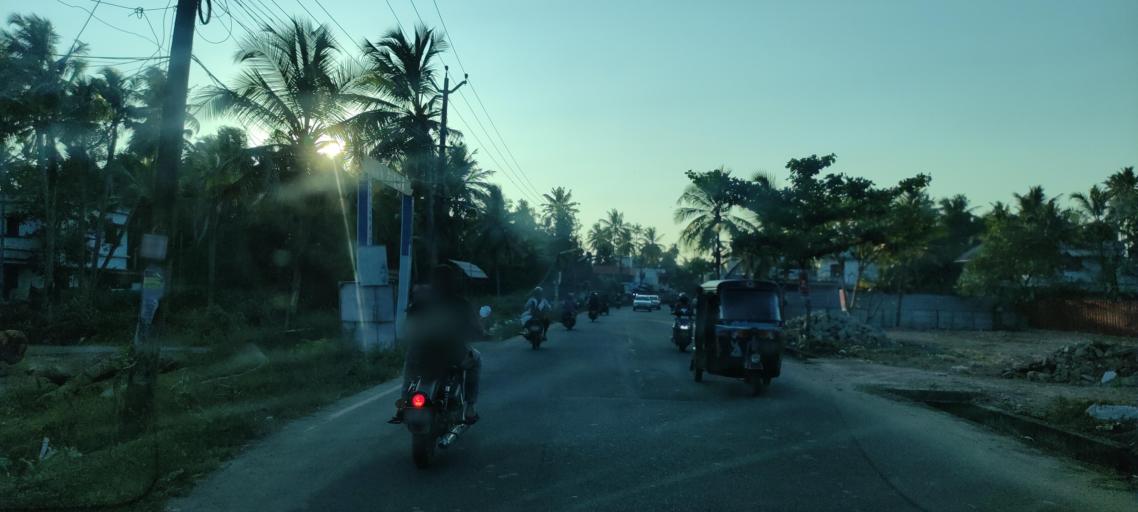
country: IN
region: Kerala
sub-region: Alappuzha
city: Kayankulam
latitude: 9.1773
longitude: 76.4885
